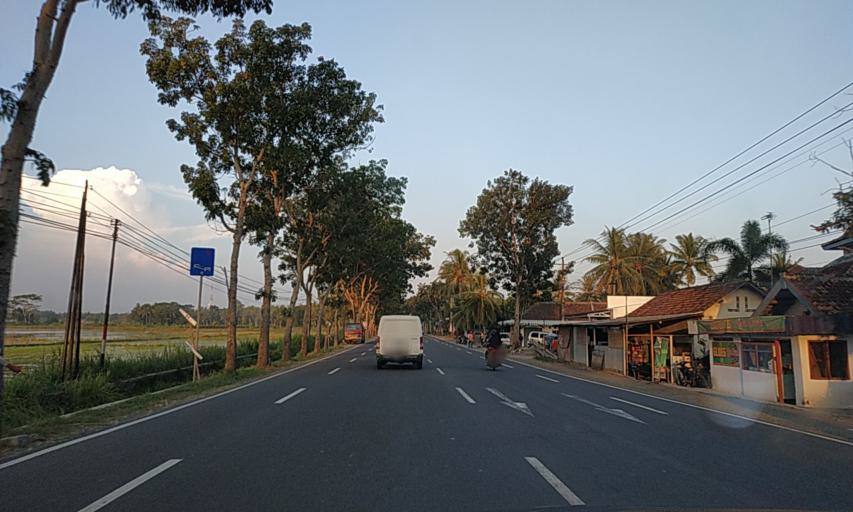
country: ID
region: Daerah Istimewa Yogyakarta
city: Srandakan
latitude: -7.8872
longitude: 110.0845
